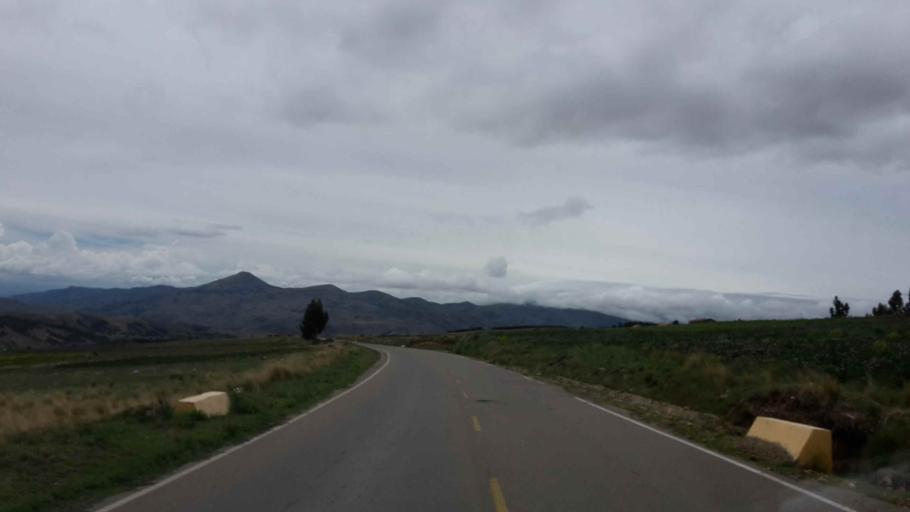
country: BO
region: Cochabamba
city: Arani
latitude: -17.4660
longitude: -65.6671
